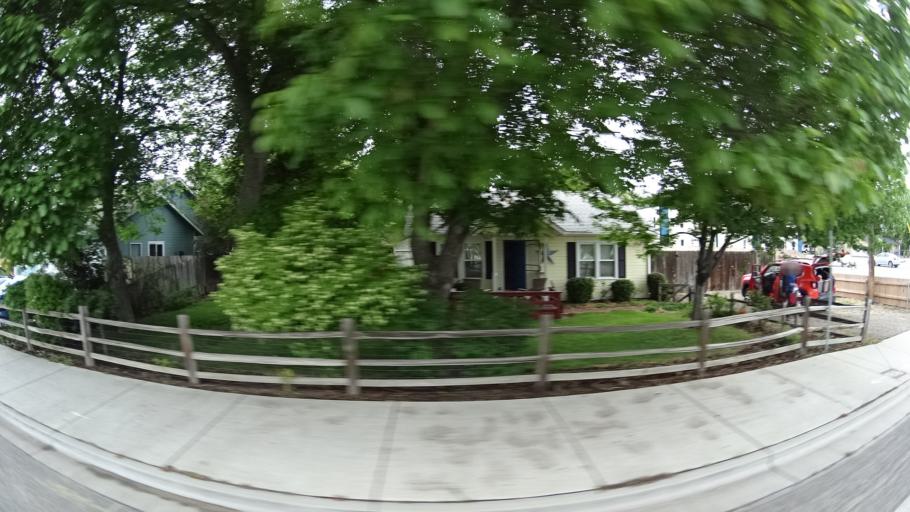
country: US
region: Idaho
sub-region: Ada County
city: Star
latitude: 43.6939
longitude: -116.4933
